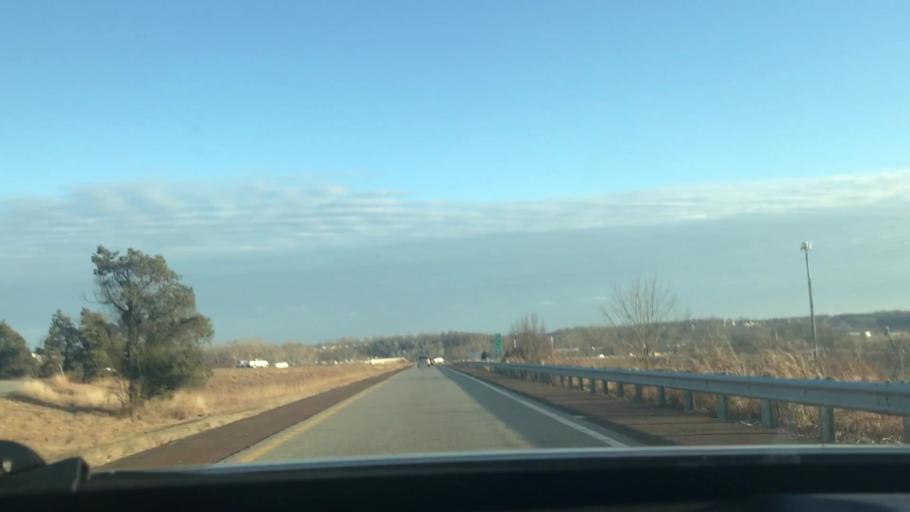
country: US
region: Missouri
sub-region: Jackson County
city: East Independence
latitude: 39.0399
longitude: -94.3647
